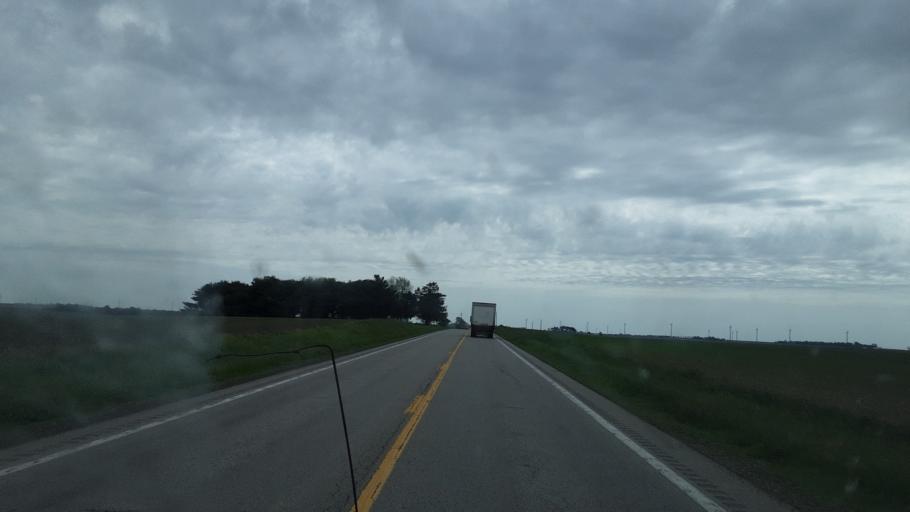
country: US
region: Illinois
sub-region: Tazewell County
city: Delavan
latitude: 40.3076
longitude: -89.4799
